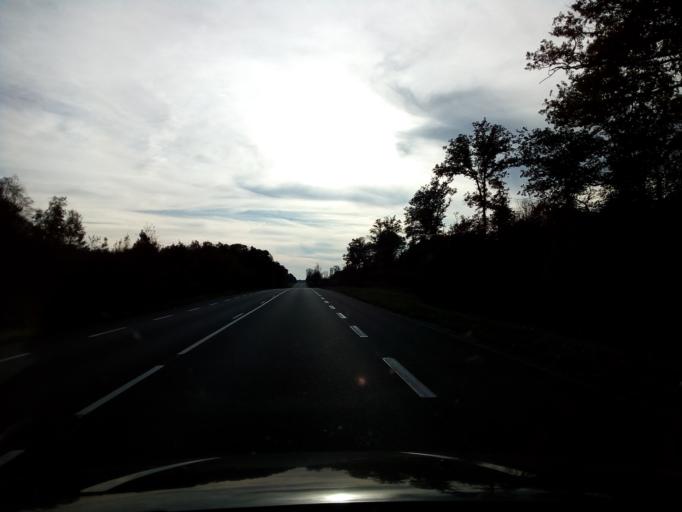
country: FR
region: Poitou-Charentes
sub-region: Departement de la Charente
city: Loubert
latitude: 45.9279
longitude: 0.5245
